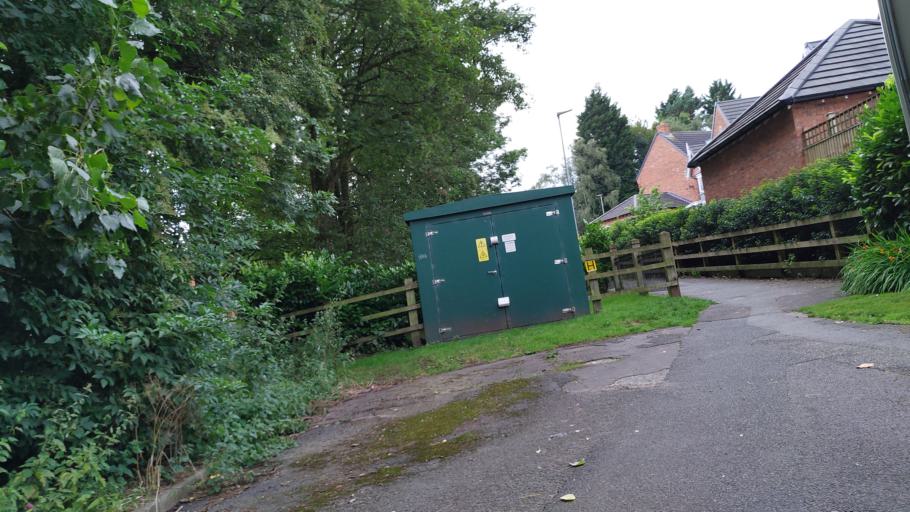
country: GB
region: England
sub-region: Lancashire
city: Chorley
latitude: 53.6392
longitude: -2.6237
